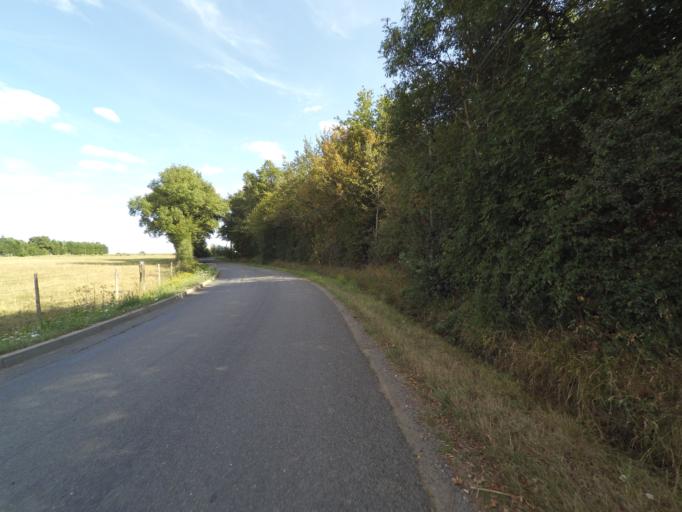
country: FR
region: Pays de la Loire
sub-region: Departement de la Loire-Atlantique
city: Vieillevigne
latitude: 46.9586
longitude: -1.4556
